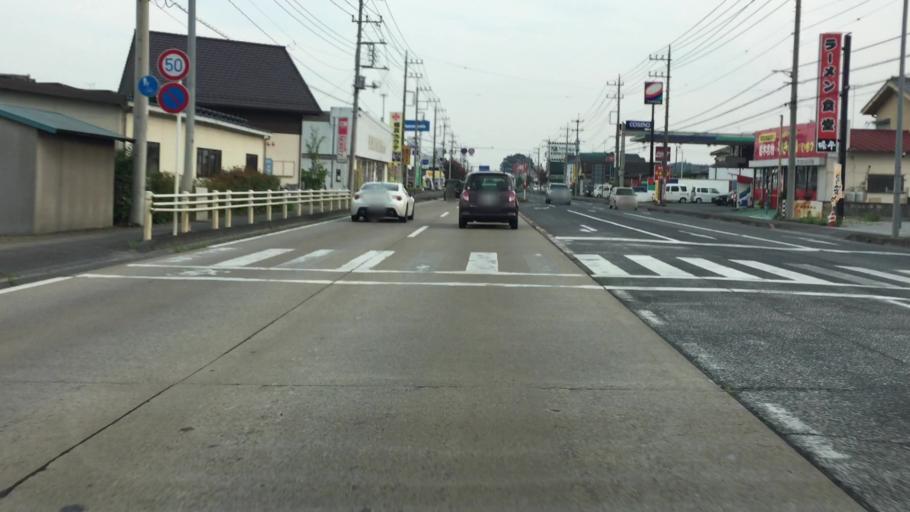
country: JP
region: Tochigi
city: Tochigi
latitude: 36.3779
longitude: 139.7160
